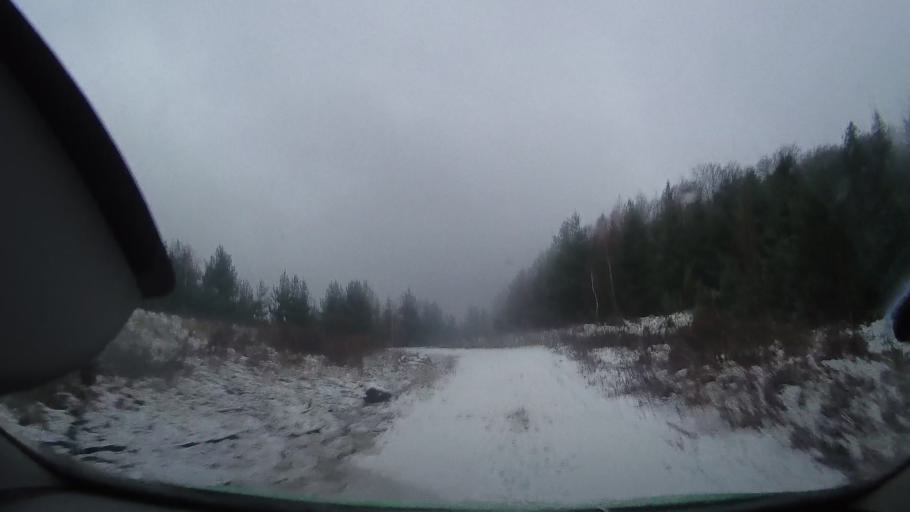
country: RO
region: Alba
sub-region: Comuna Avram Iancu
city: Avram Iancu
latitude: 46.3066
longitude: 22.7976
